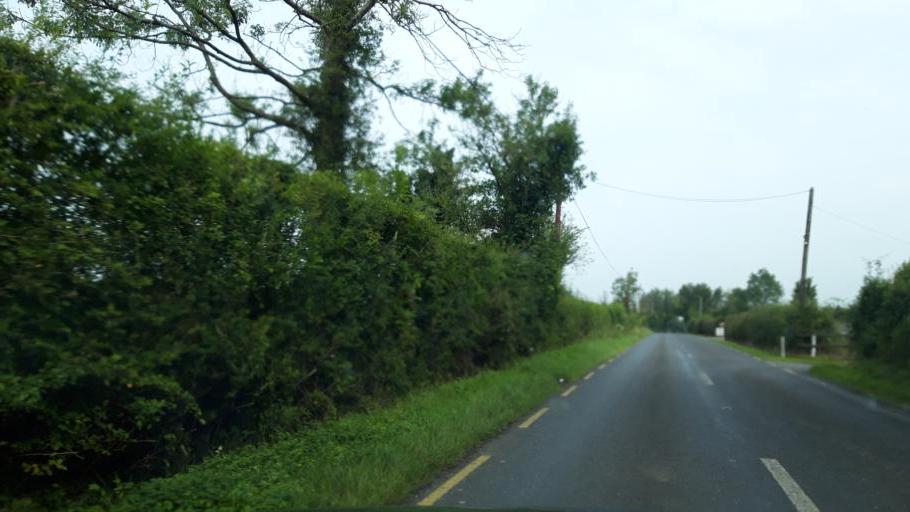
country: IE
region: Leinster
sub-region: Kilkenny
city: Callan
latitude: 52.5366
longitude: -7.5216
